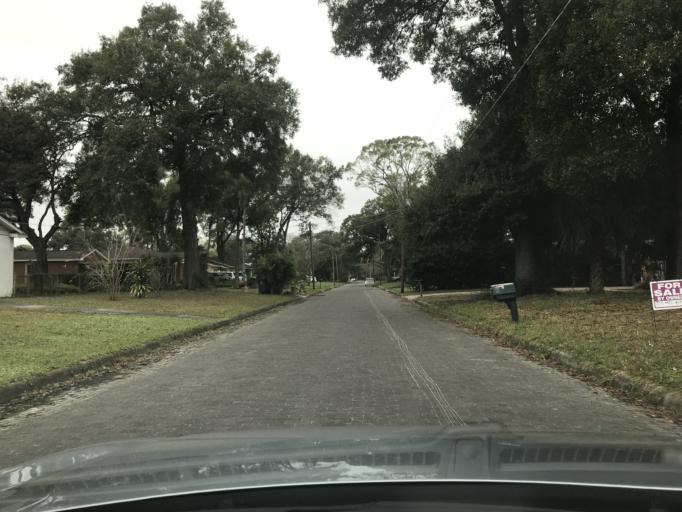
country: US
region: Florida
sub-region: Hillsborough County
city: Tampa
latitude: 27.9772
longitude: -82.4717
